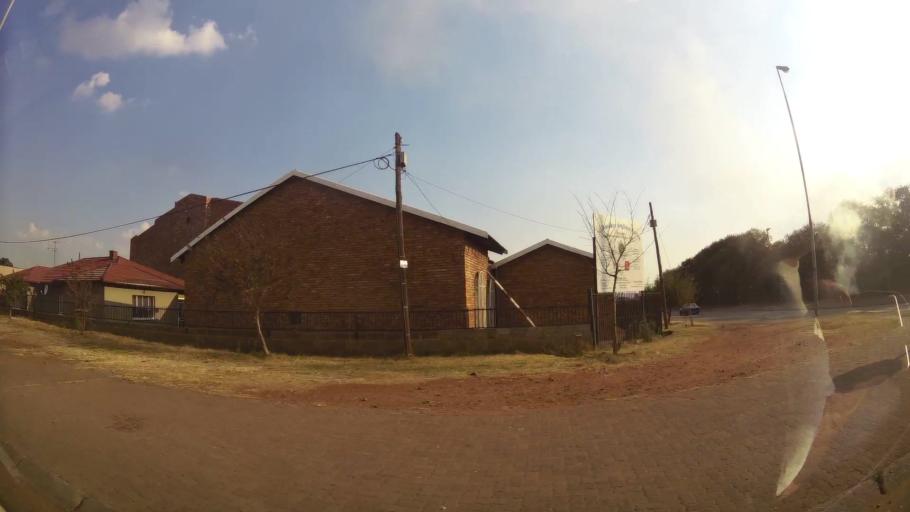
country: ZA
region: Gauteng
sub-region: Ekurhuleni Metropolitan Municipality
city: Germiston
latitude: -26.3546
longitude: 28.2044
